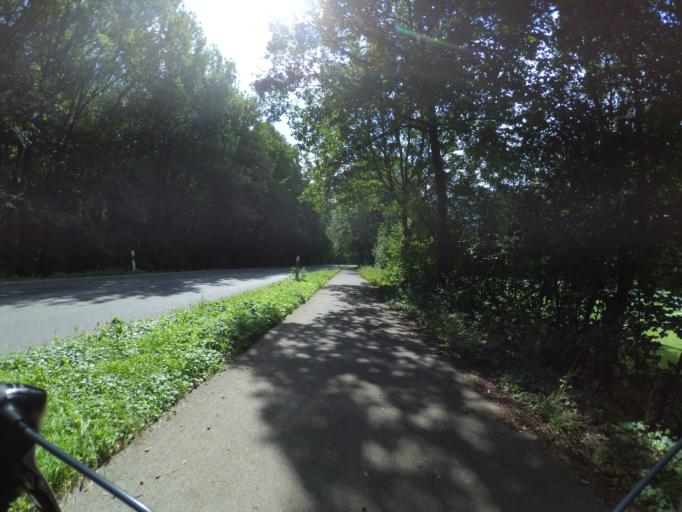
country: DE
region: North Rhine-Westphalia
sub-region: Regierungsbezirk Koln
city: Langerwehe
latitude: 50.8052
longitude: 6.3503
